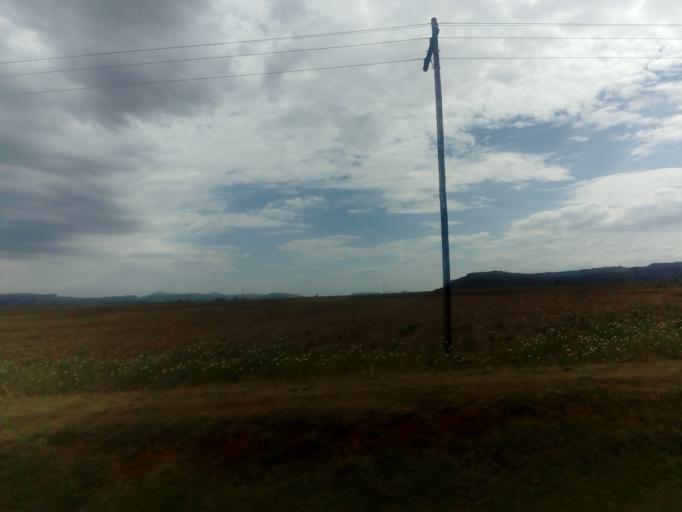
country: LS
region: Leribe
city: Maputsoe
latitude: -28.9423
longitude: 27.9535
